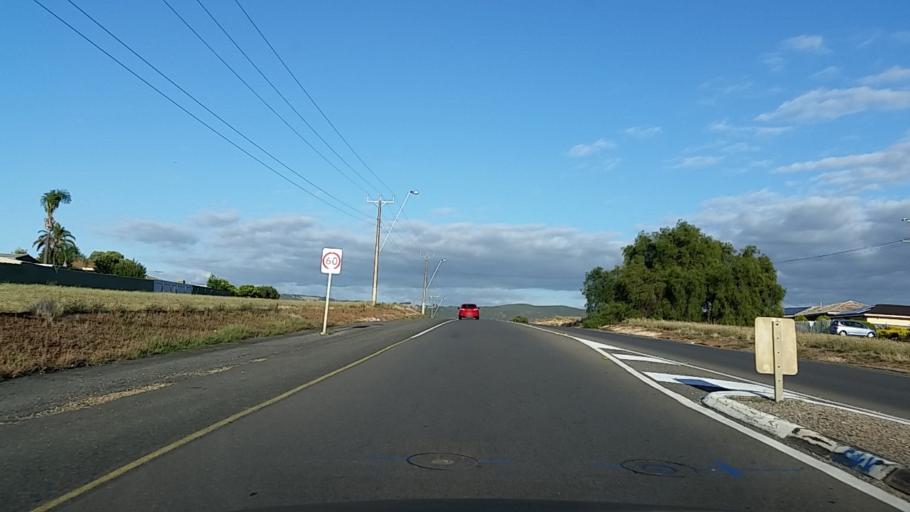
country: AU
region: South Australia
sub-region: Tea Tree Gully
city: Modbury
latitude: -34.8284
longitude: 138.6817
